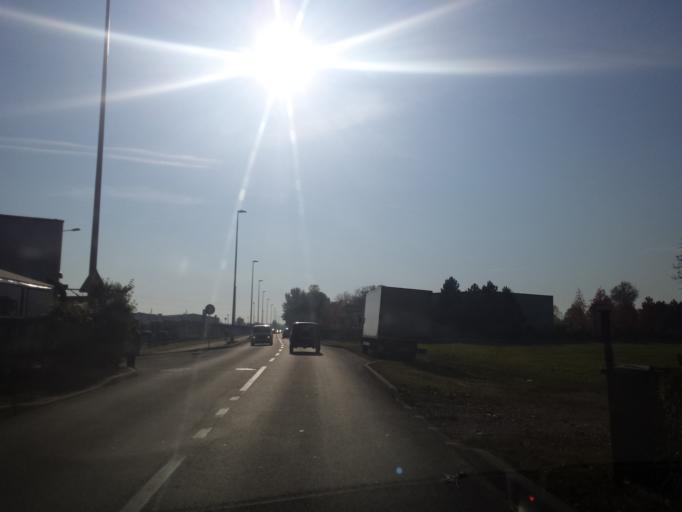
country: HR
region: Grad Zagreb
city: Stenjevec
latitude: 45.8027
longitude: 15.8747
